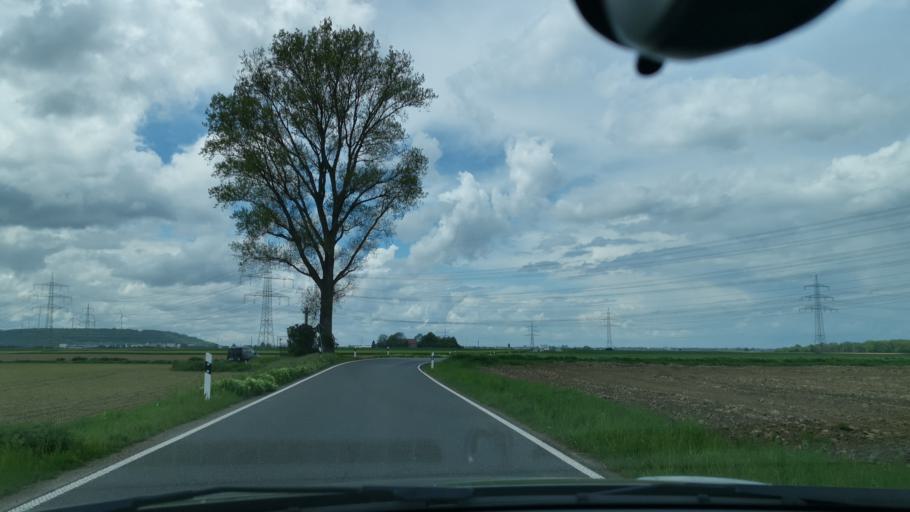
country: DE
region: North Rhine-Westphalia
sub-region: Regierungsbezirk Dusseldorf
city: Rommerskirchen
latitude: 51.0870
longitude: 6.6781
